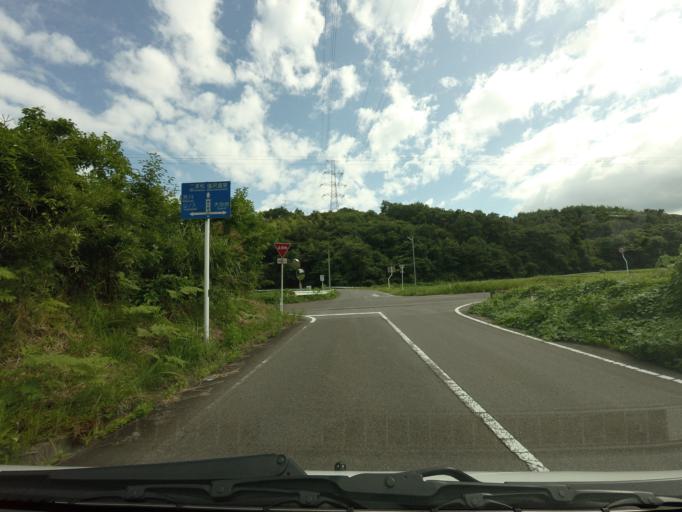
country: JP
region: Fukushima
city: Nihommatsu
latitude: 37.6368
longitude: 140.4109
